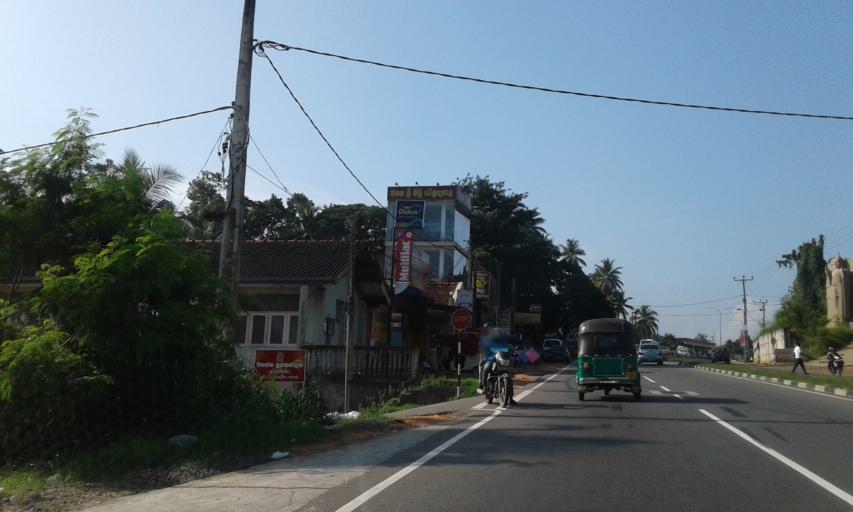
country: LK
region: Western
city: Gampaha
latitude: 7.0372
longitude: 79.9918
